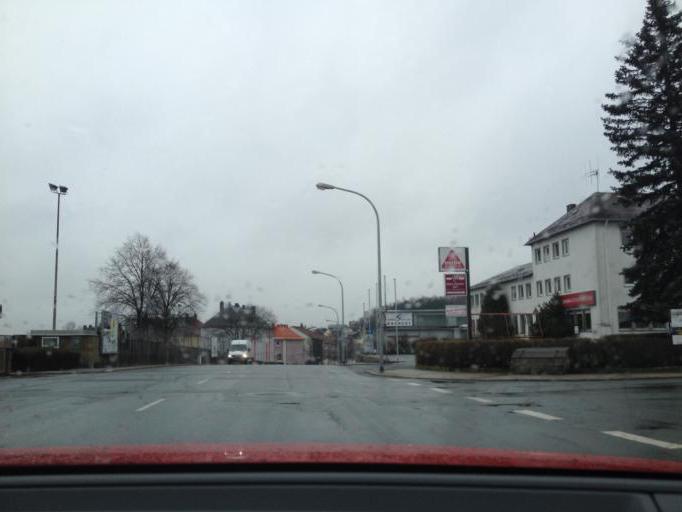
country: DE
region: Bavaria
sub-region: Upper Franconia
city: Hof
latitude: 50.3039
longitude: 11.9218
